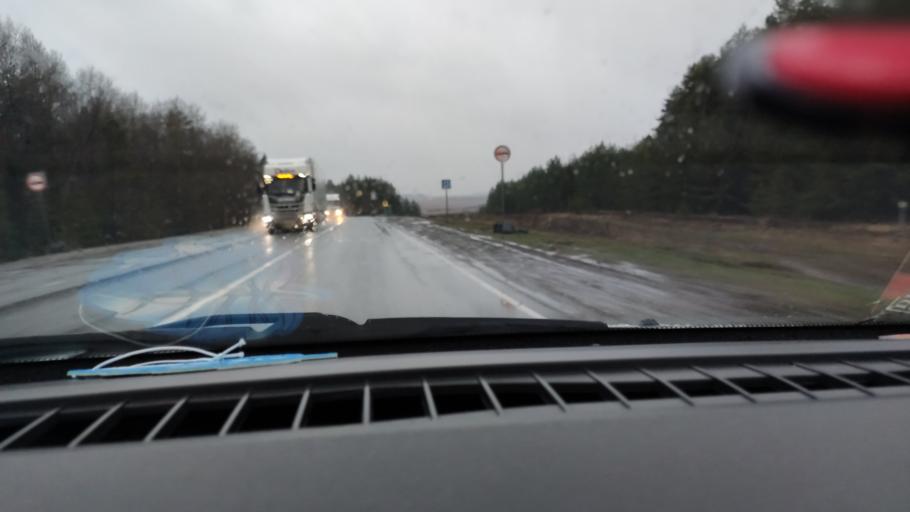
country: RU
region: Tatarstan
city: Mendeleyevsk
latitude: 55.9439
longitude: 52.2939
